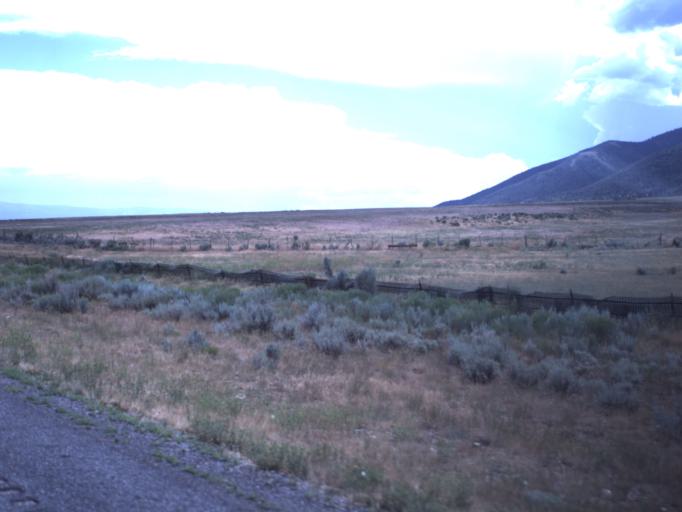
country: US
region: Utah
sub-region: Sanpete County
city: Fountain Green
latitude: 39.6843
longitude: -111.6766
